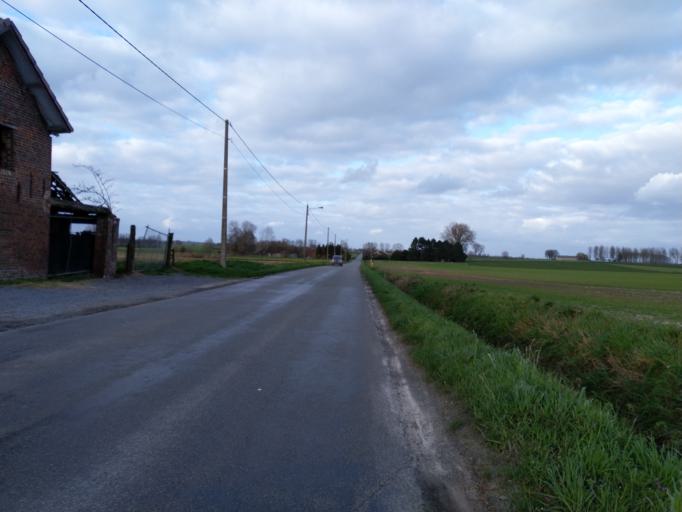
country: BE
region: Wallonia
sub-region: Province du Hainaut
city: Jurbise
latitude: 50.5435
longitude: 3.9736
